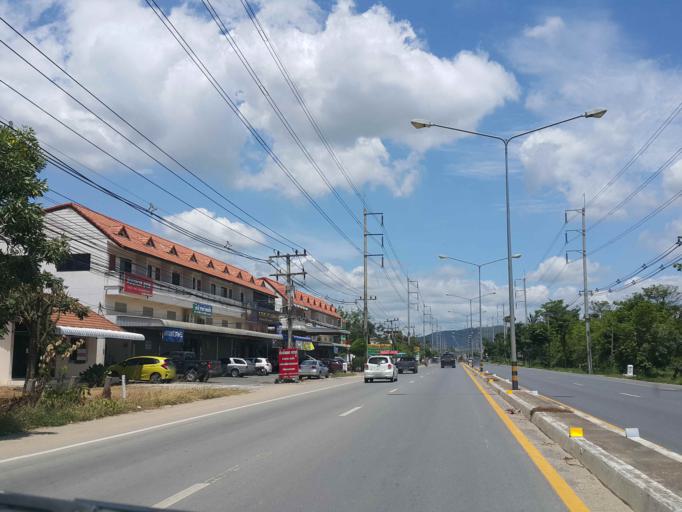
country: TH
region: Chiang Mai
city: Hang Dong
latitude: 18.7237
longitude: 98.9356
